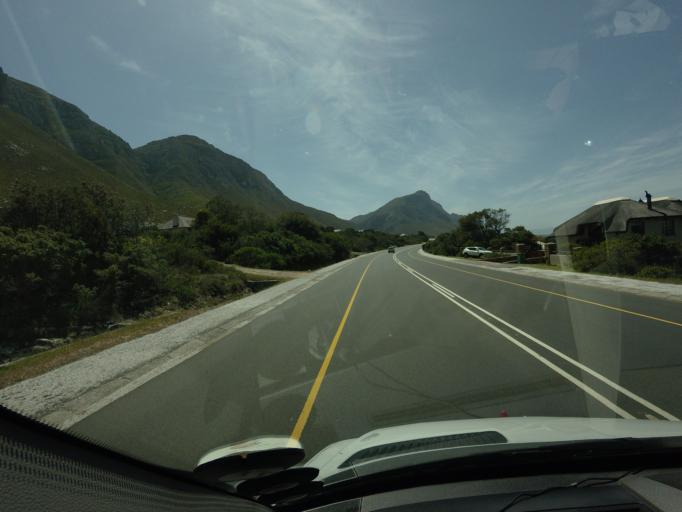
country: ZA
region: Western Cape
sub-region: Overberg District Municipality
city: Grabouw
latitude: -34.3543
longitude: 18.9055
